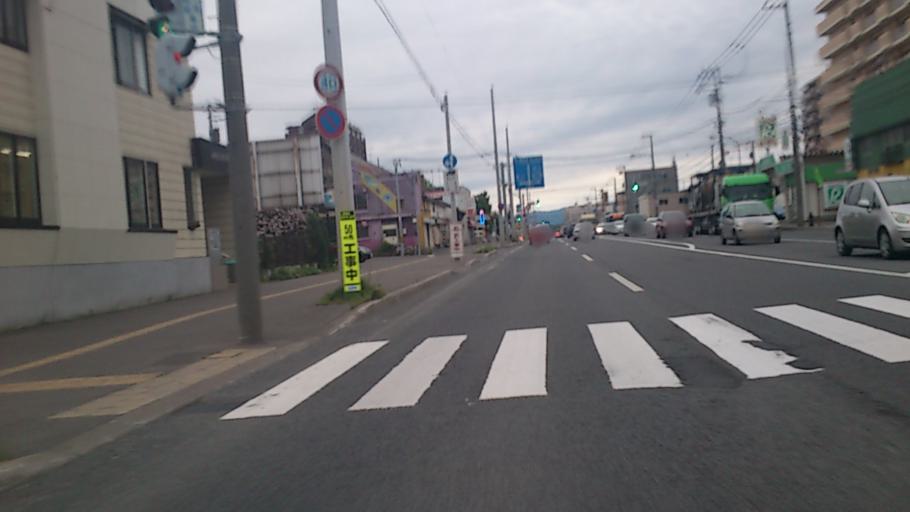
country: JP
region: Hokkaido
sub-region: Asahikawa-shi
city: Asahikawa
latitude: 43.7674
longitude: 142.3797
